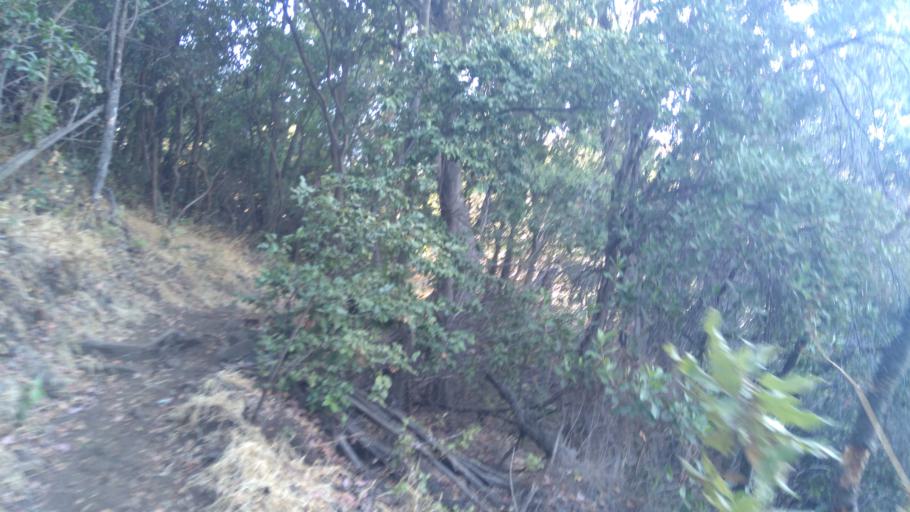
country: CL
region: Santiago Metropolitan
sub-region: Provincia de Cordillera
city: Puente Alto
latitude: -33.7125
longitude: -70.4575
